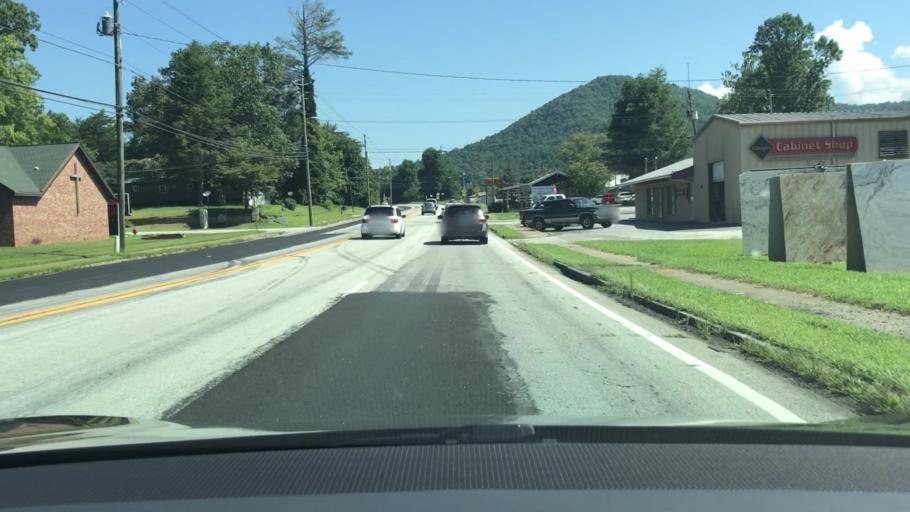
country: US
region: Georgia
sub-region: Rabun County
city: Mountain City
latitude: 34.9166
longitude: -83.3861
